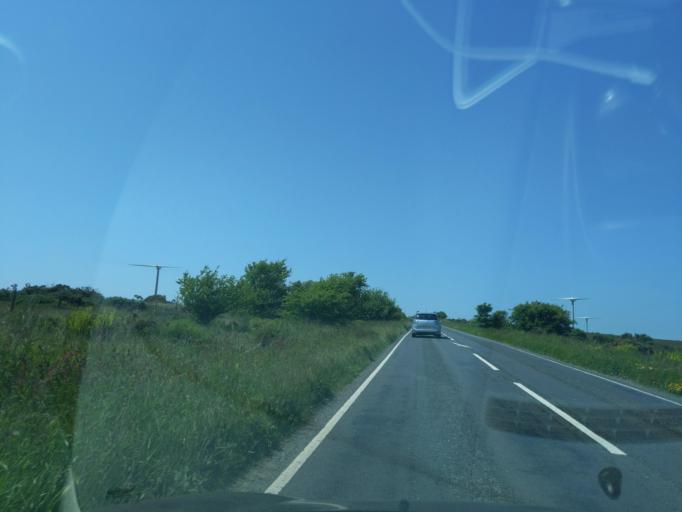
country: GB
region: England
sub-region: Cornwall
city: Trewen
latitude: 50.6411
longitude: -4.5228
